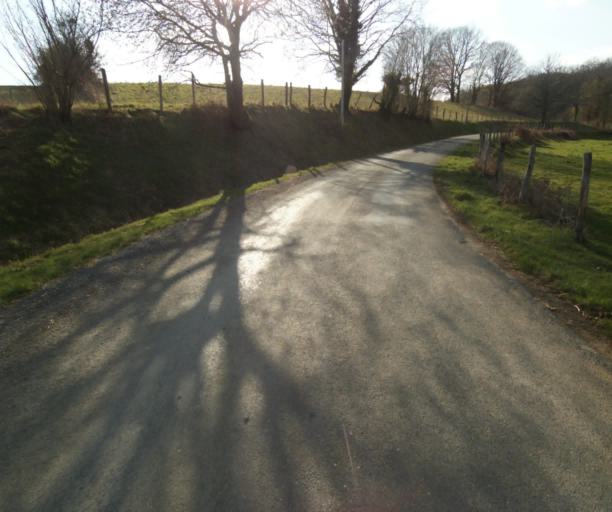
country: FR
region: Limousin
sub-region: Departement de la Correze
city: Saint-Mexant
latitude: 45.3410
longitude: 1.6157
